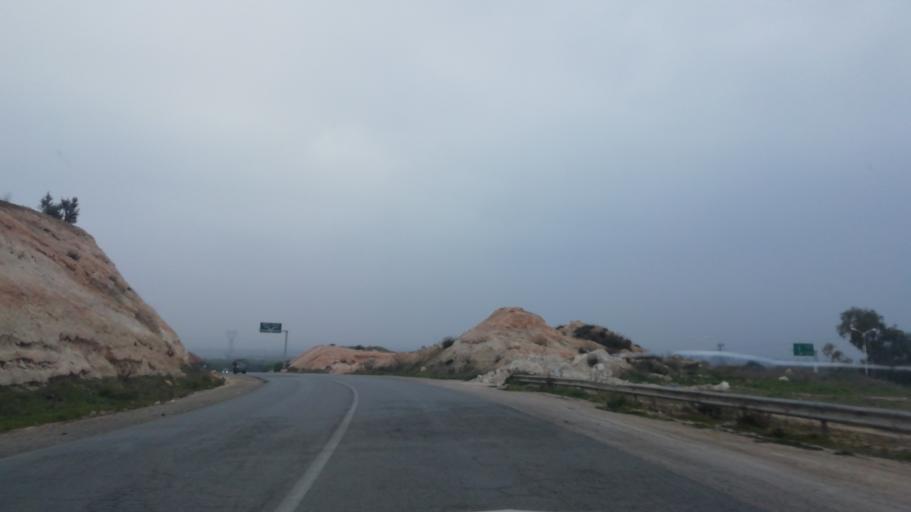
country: DZ
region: Mascara
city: Mascara
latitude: 35.3840
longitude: 0.1610
